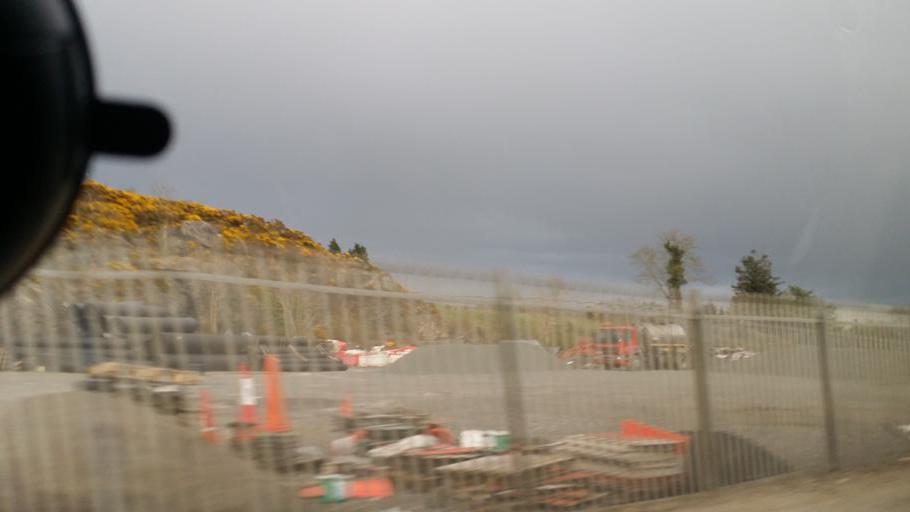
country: IE
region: Ulster
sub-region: An Cabhan
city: Virginia
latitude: 53.8509
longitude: -7.1015
